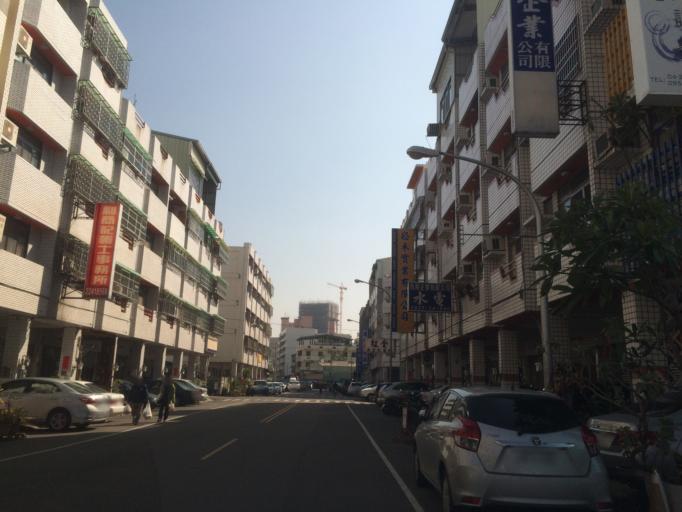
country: TW
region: Taiwan
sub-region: Taichung City
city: Taichung
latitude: 24.1776
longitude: 120.6953
